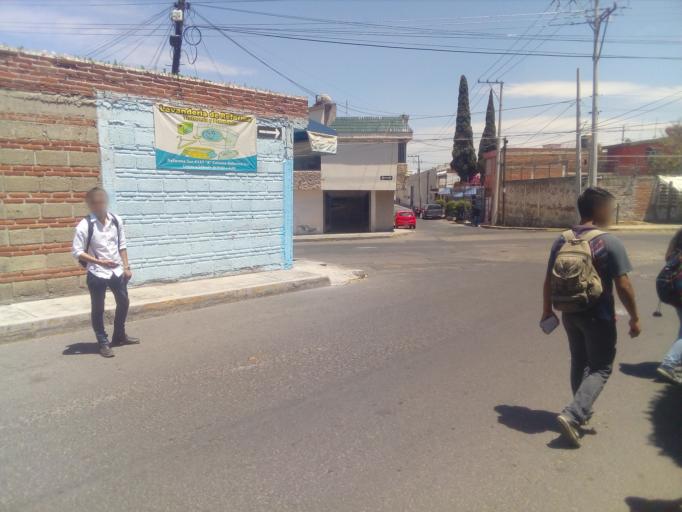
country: MX
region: Puebla
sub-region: San Pedro Cholula
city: Santiago Momoxpan
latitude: 19.0616
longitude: -98.2331
